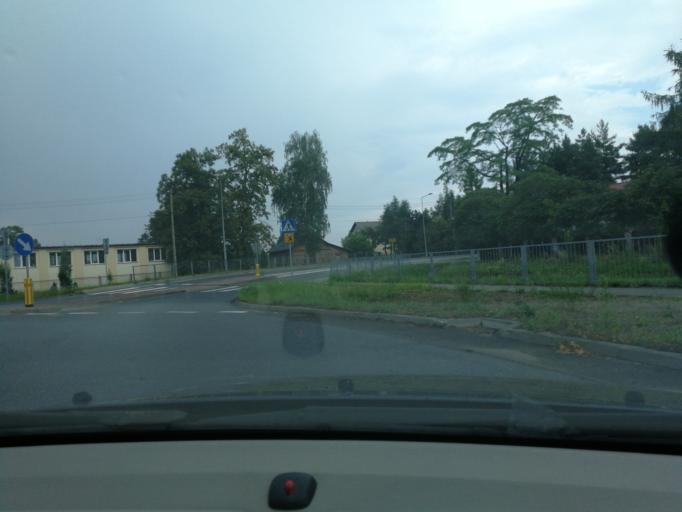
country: PL
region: Masovian Voivodeship
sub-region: Powiat zyrardowski
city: Radziejowice
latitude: 52.0043
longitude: 20.5562
